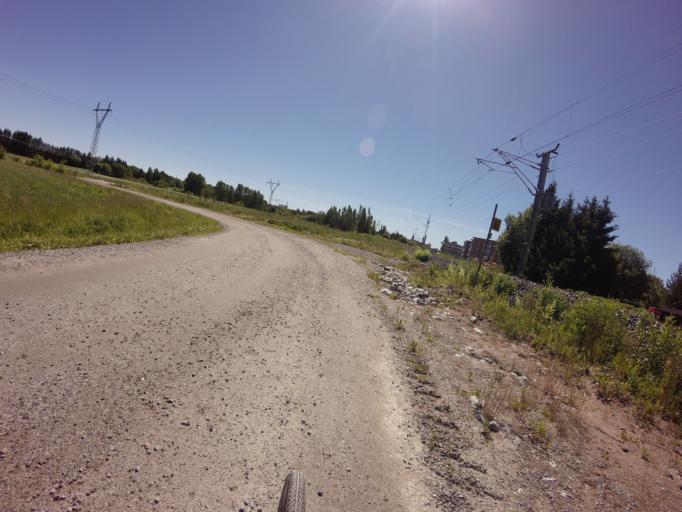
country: FI
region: Varsinais-Suomi
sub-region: Turku
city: Turku
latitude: 60.4689
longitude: 22.2858
